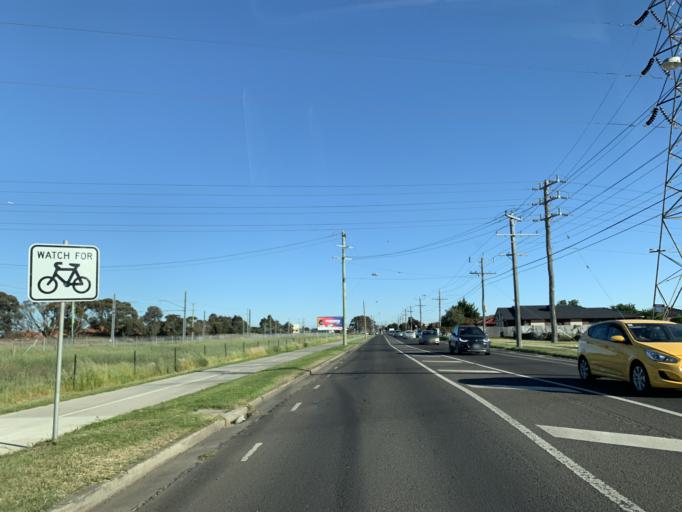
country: AU
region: Victoria
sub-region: Brimbank
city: Sunshine North
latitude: -37.7633
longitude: 144.8145
